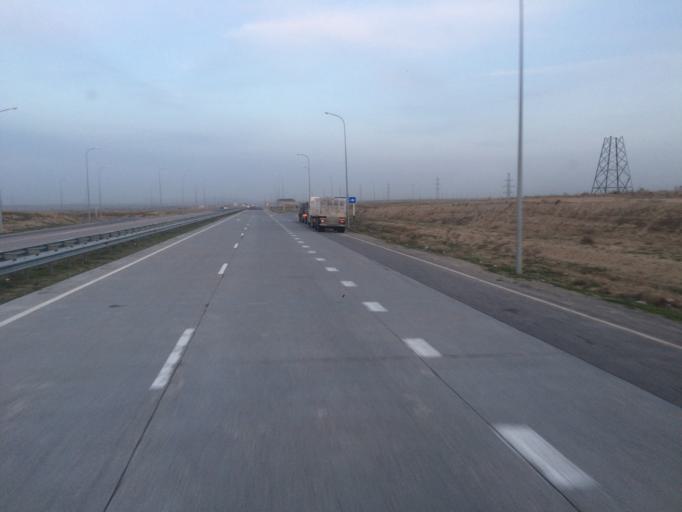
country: KZ
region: Ongtustik Qazaqstan
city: Shymkent
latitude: 42.4524
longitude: 69.6282
